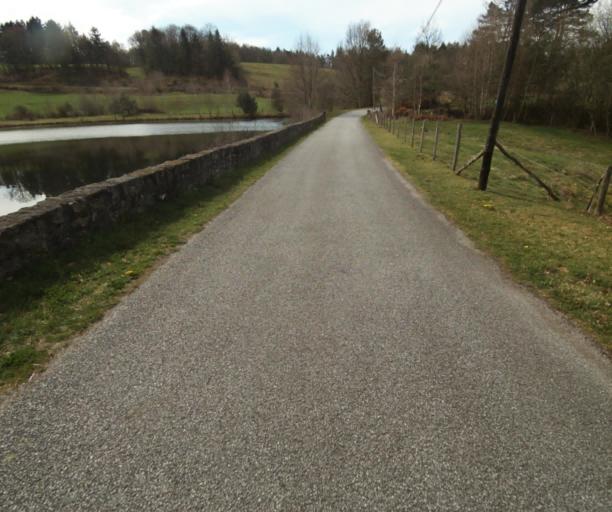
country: FR
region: Limousin
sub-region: Departement de la Correze
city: Correze
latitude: 45.3803
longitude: 1.8952
